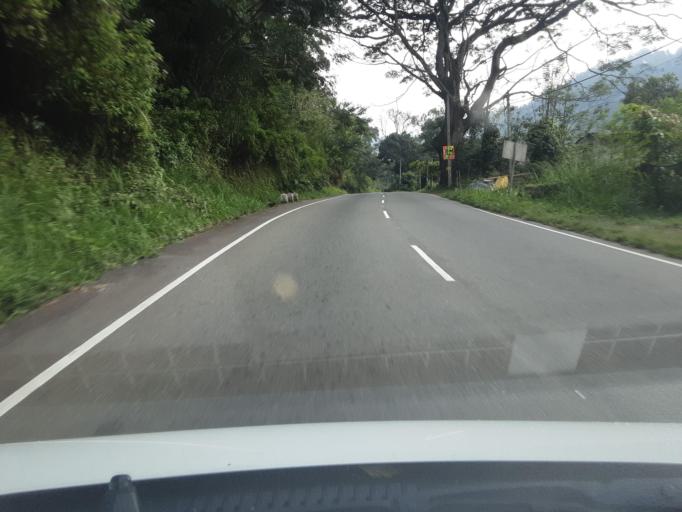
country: LK
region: Uva
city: Badulla
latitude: 6.9447
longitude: 81.0173
